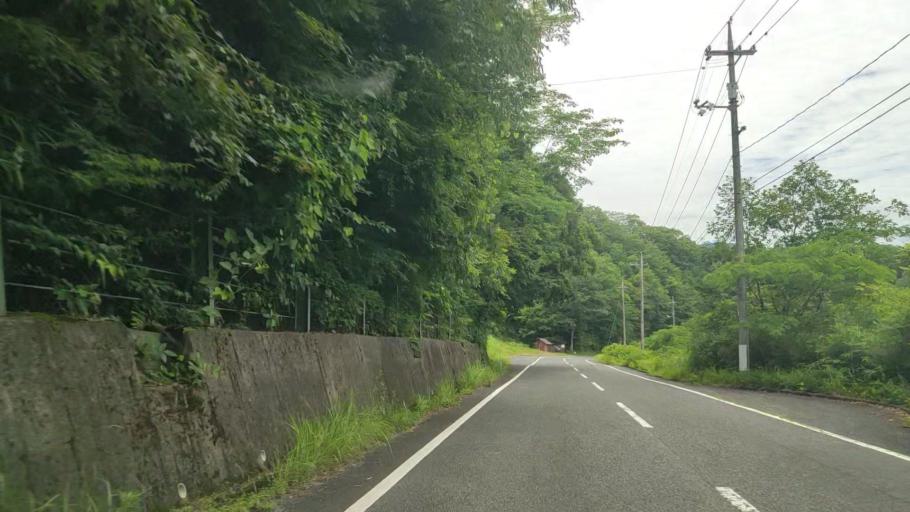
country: JP
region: Okayama
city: Tsuyama
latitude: 35.0989
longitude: 134.2744
